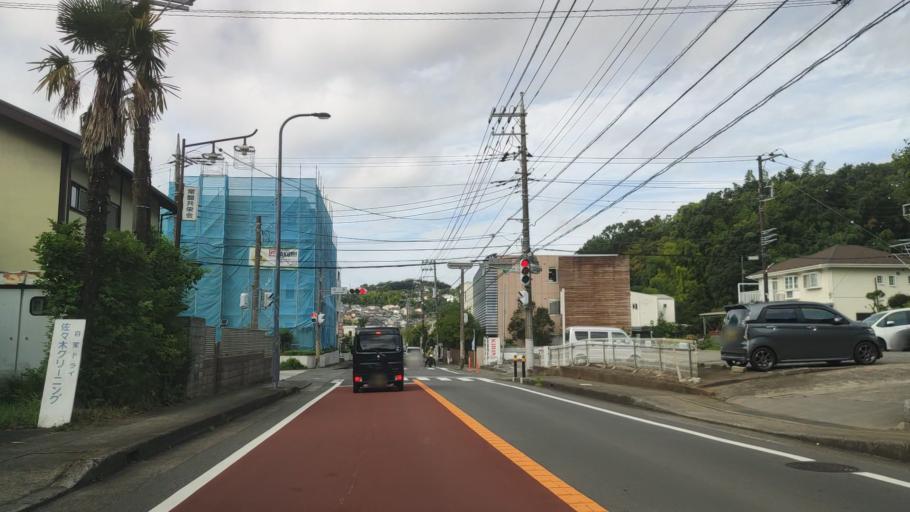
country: JP
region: Kanagawa
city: Kamakura
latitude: 35.3224
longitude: 139.5311
